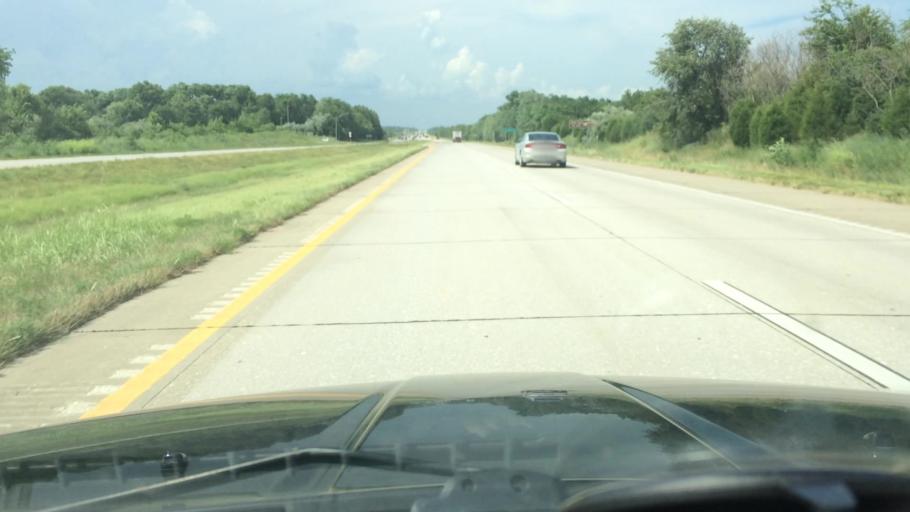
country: US
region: Missouri
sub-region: Henry County
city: Clinton
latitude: 38.2618
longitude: -93.7603
